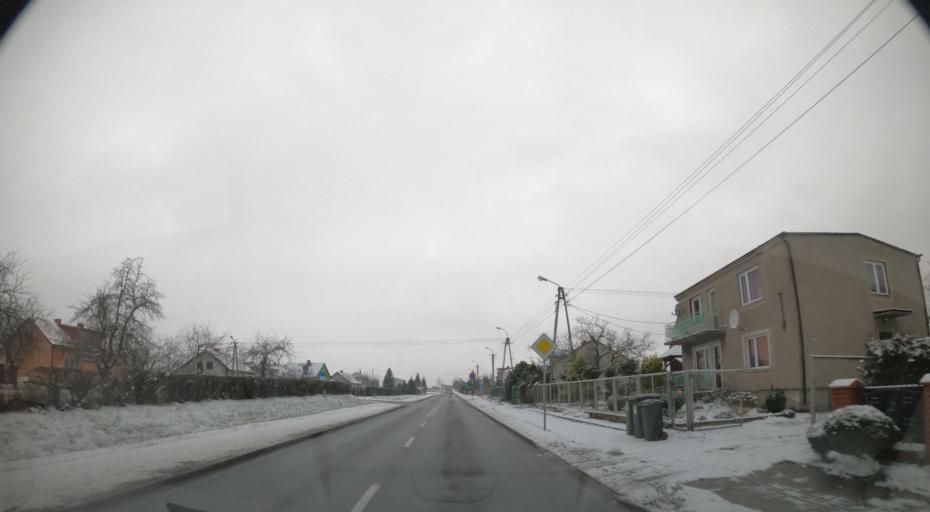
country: PL
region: Kujawsko-Pomorskie
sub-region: Powiat lipnowski
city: Wielgie
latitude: 52.7448
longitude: 19.2521
